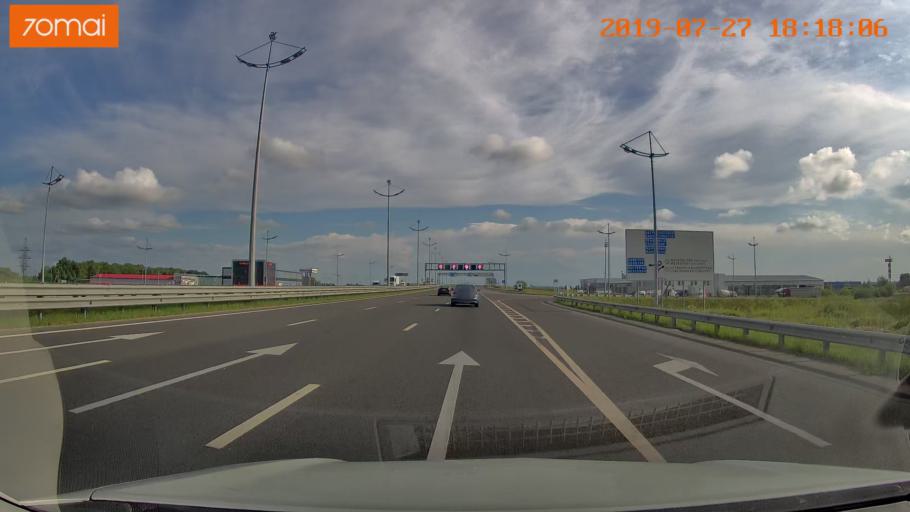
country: RU
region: Kaliningrad
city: Bol'shoe Isakovo
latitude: 54.7108
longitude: 20.5971
